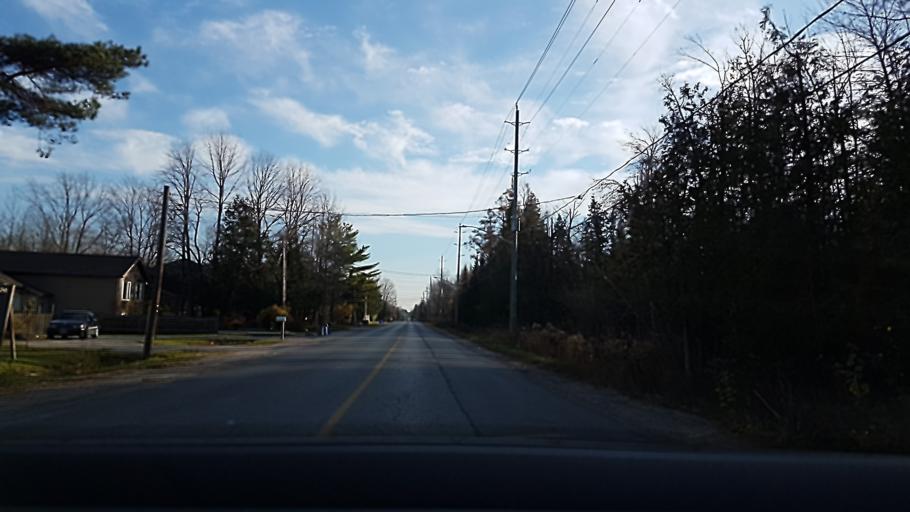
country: CA
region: Ontario
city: Innisfil
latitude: 44.3450
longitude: -79.5470
